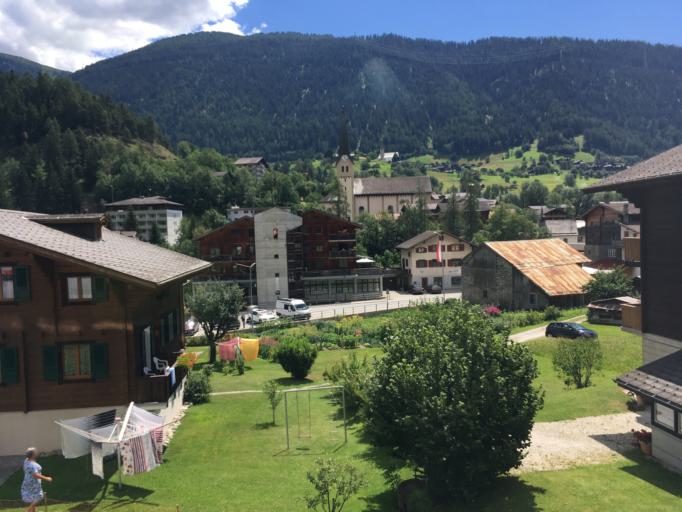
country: CH
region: Valais
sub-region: Goms District
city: Fiesch
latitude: 46.4048
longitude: 8.1329
